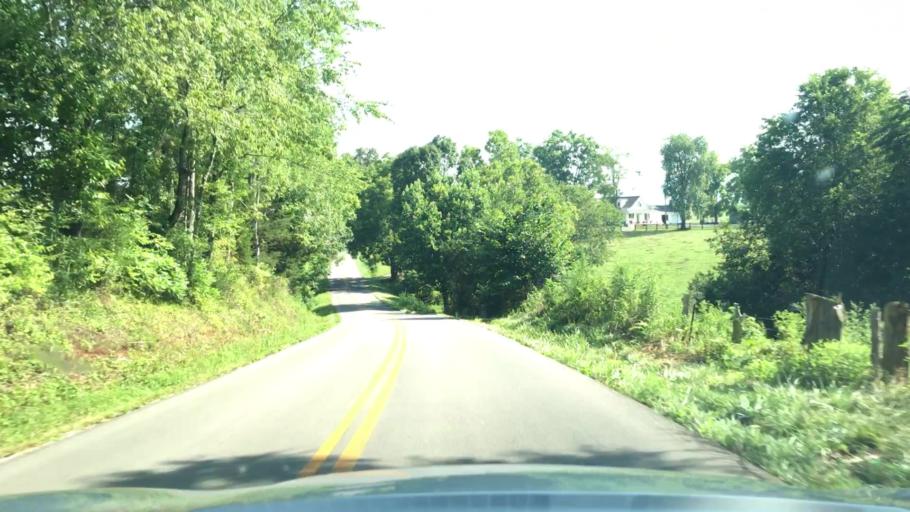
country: US
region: Kentucky
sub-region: Clinton County
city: Albany
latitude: 36.6380
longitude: -85.0834
